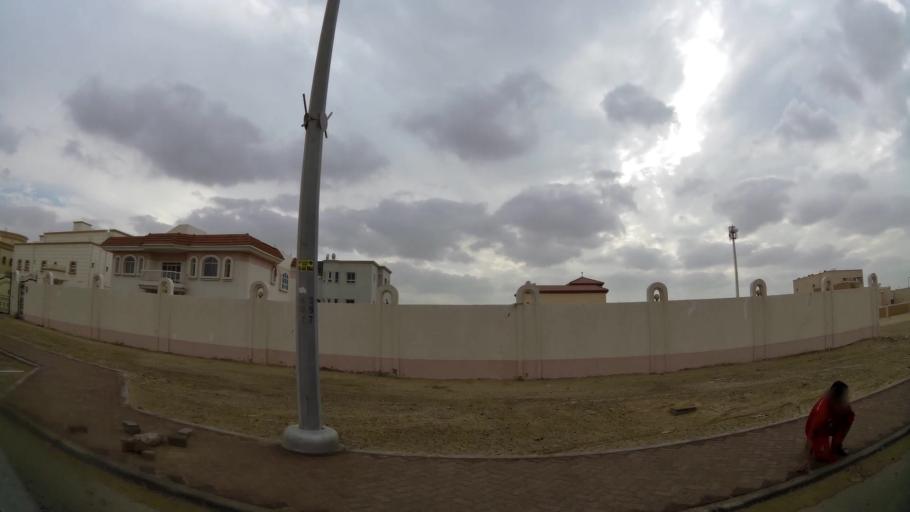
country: AE
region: Abu Dhabi
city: Abu Dhabi
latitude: 24.3530
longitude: 54.6285
